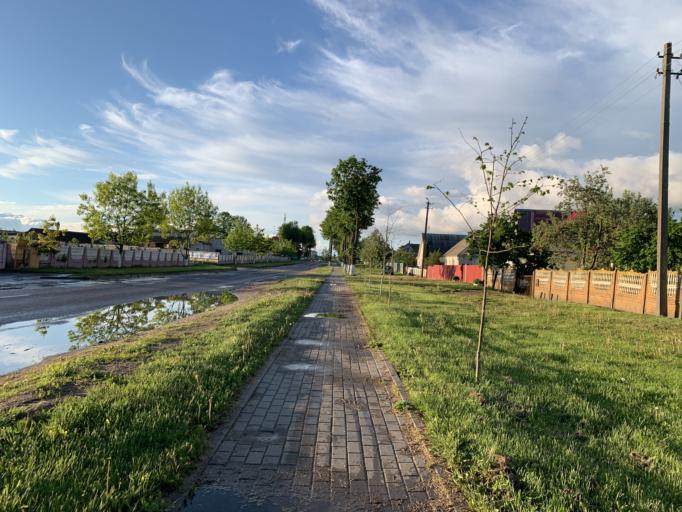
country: BY
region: Minsk
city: Nyasvizh
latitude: 53.2101
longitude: 26.6968
